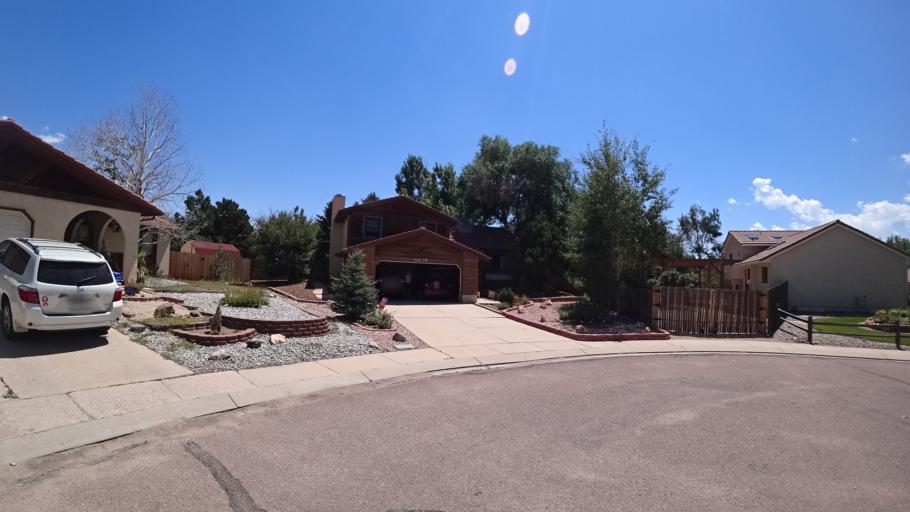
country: US
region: Colorado
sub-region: El Paso County
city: Black Forest
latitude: 38.9542
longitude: -104.7529
